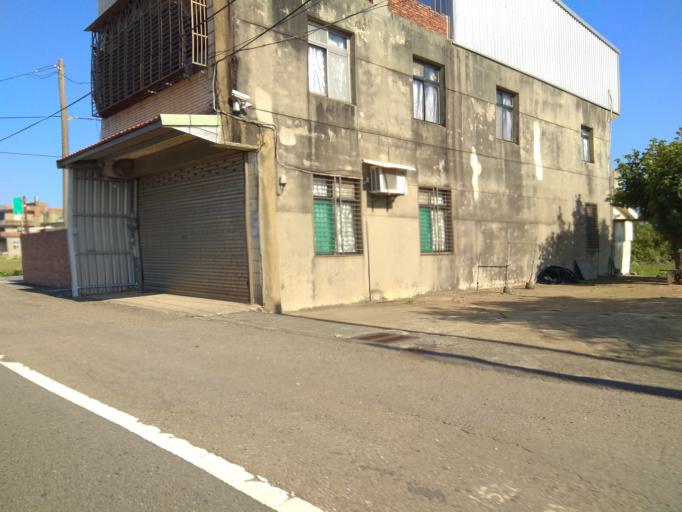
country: TW
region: Taiwan
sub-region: Hsinchu
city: Zhubei
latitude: 25.0042
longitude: 121.0403
